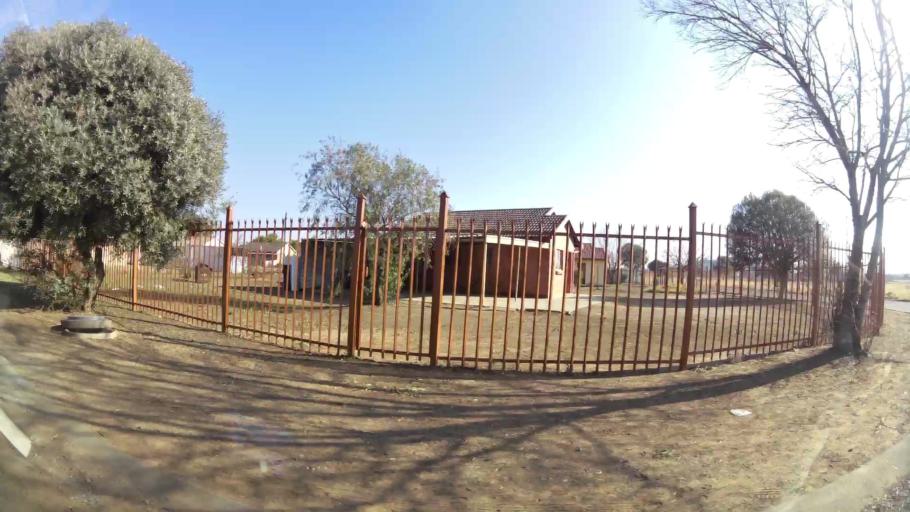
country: ZA
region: Orange Free State
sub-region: Mangaung Metropolitan Municipality
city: Bloemfontein
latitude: -29.1835
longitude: 26.1763
